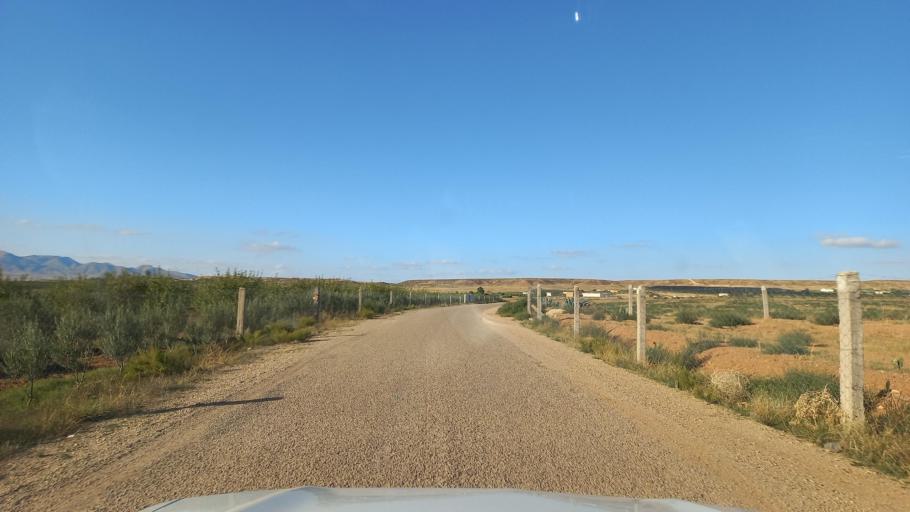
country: TN
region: Al Qasrayn
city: Sbiba
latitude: 35.3378
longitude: 9.1191
